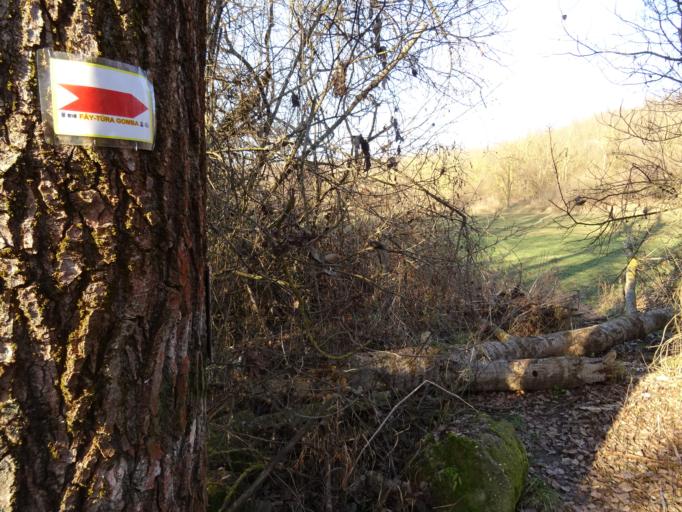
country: HU
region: Pest
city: Uri
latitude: 47.4002
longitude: 19.5009
